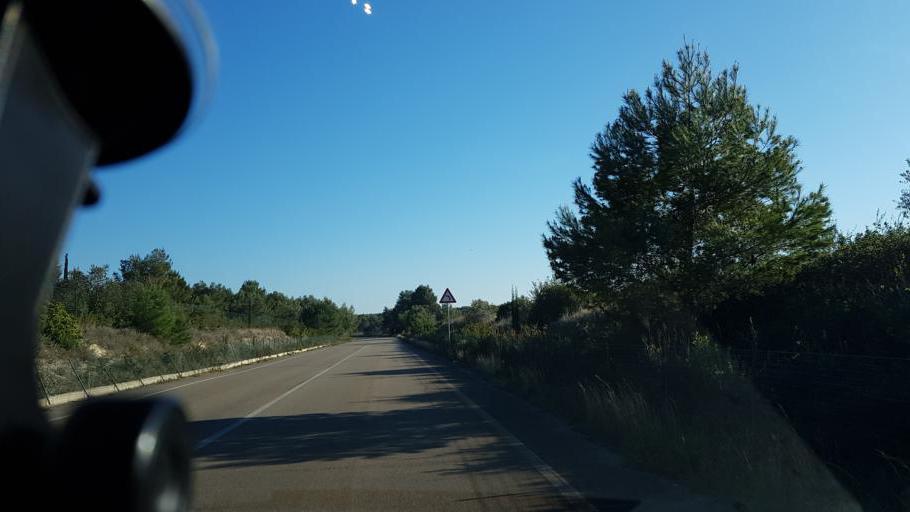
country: IT
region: Apulia
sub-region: Provincia di Lecce
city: Merine
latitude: 40.4018
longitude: 18.2496
